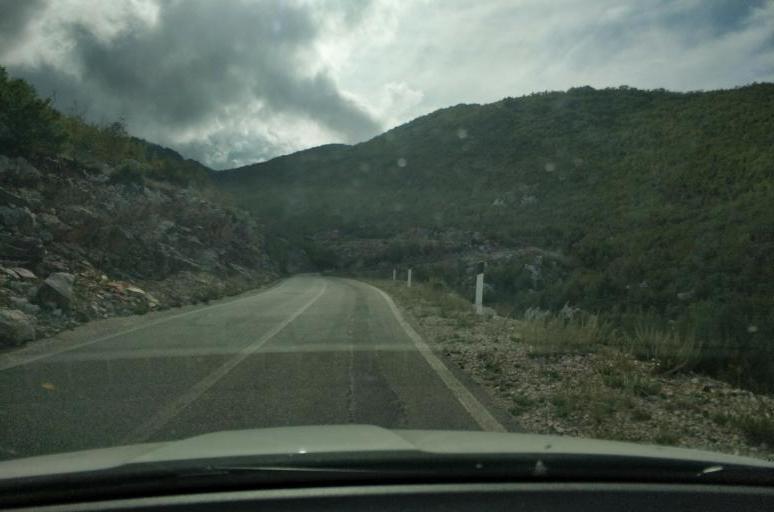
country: AL
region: Durres
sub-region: Rrethi i Krujes
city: Kruje
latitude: 41.5278
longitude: 19.7972
